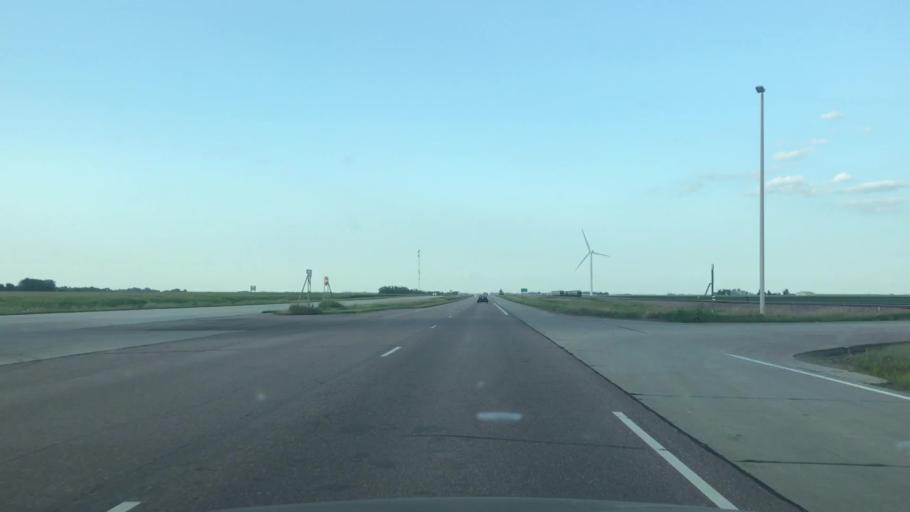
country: US
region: Minnesota
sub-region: Nobles County
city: Worthington
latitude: 43.7104
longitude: -95.4533
